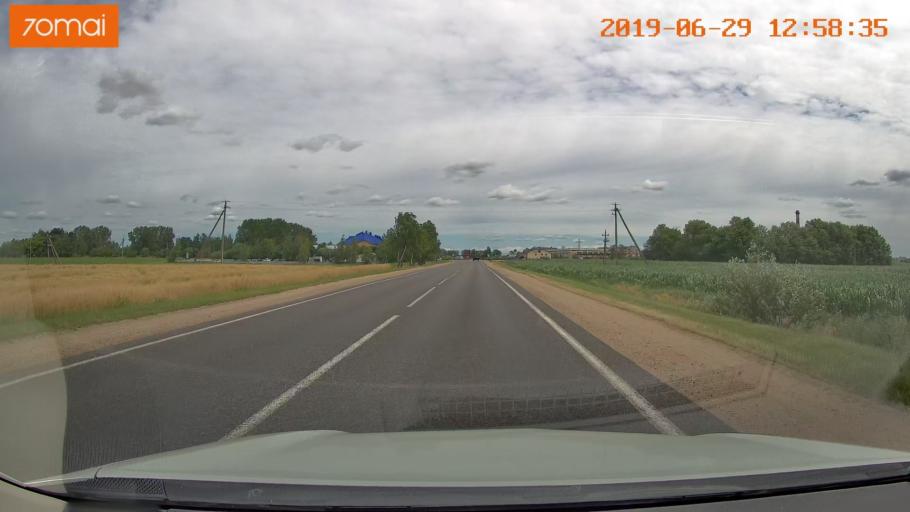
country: BY
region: Minsk
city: Slutsk
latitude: 53.0505
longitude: 27.5409
